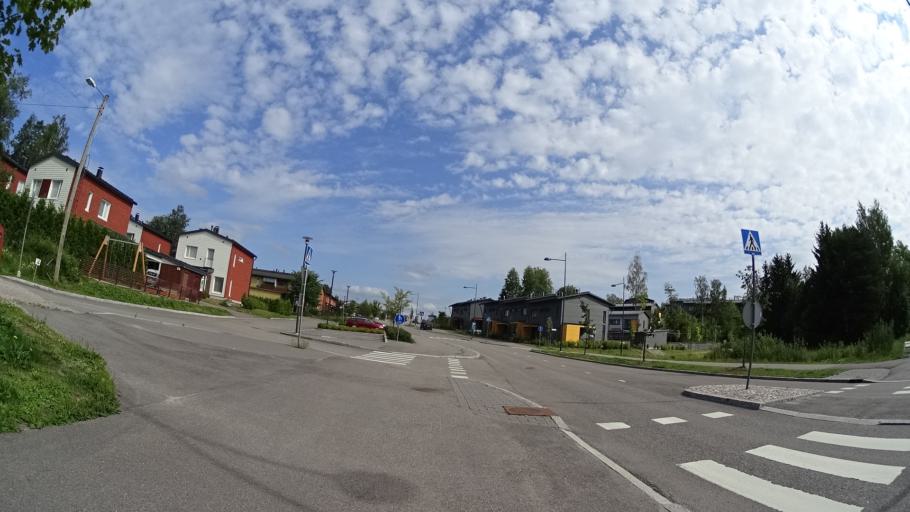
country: FI
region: Uusimaa
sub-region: Helsinki
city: Espoo
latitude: 60.1931
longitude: 24.5927
